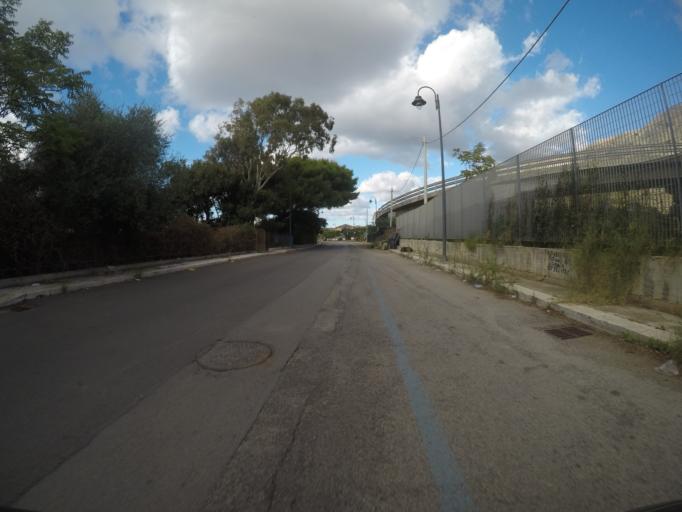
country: IT
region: Sicily
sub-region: Palermo
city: Isola delle Femmine
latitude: 38.1886
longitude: 13.2443
